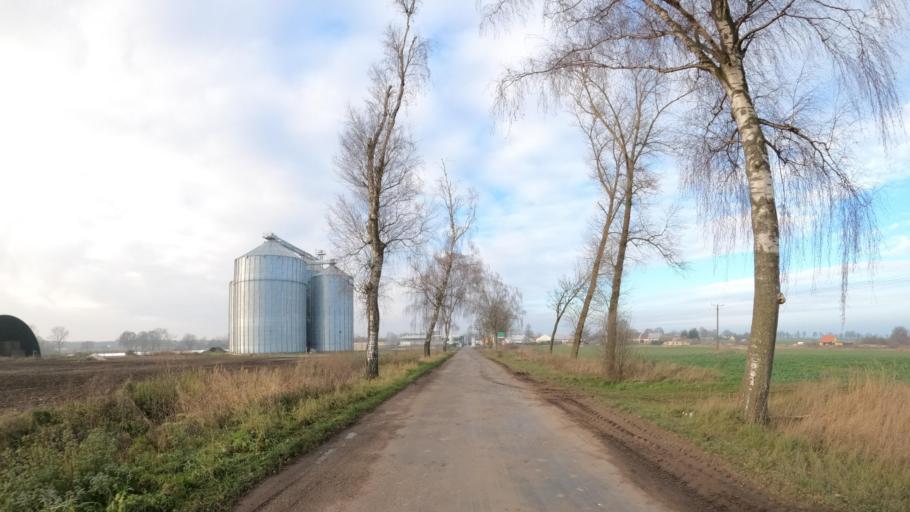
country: PL
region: West Pomeranian Voivodeship
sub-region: Powiat goleniowski
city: Osina
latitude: 53.5799
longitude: 15.0854
